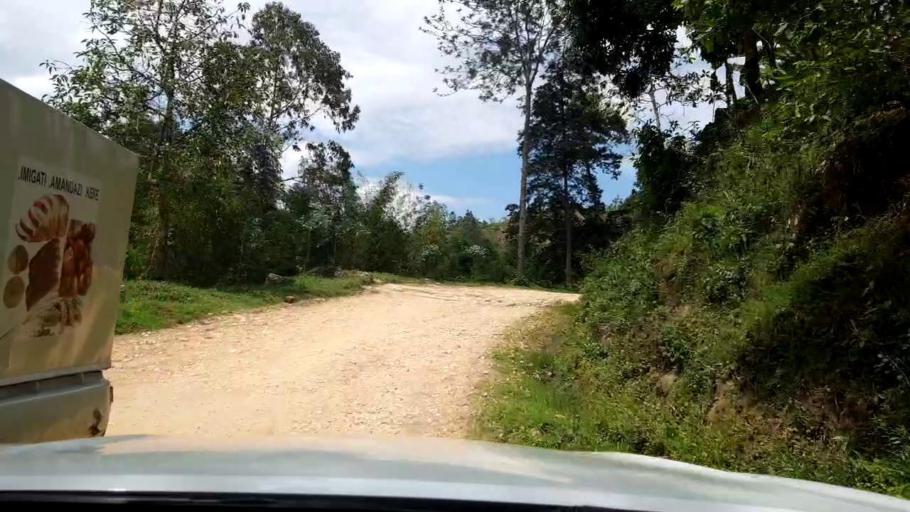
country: RW
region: Southern Province
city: Gitarama
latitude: -1.9282
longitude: 29.6506
